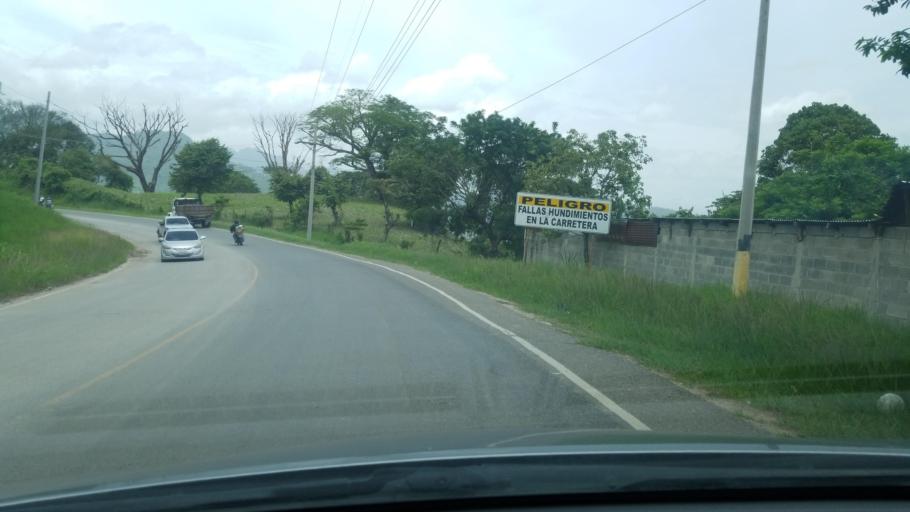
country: HN
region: Copan
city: Santa Rosa de Copan
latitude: 14.7387
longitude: -88.7753
